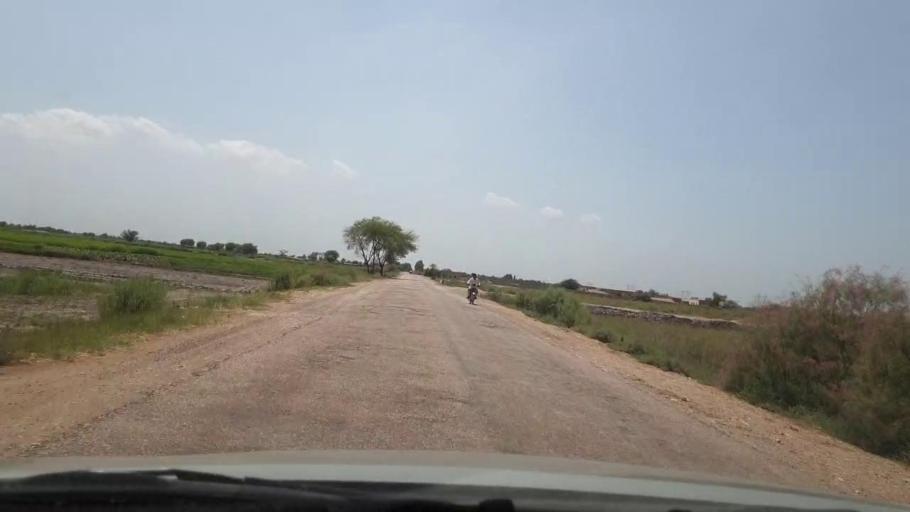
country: PK
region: Sindh
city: Rohri
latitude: 27.6695
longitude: 69.0701
